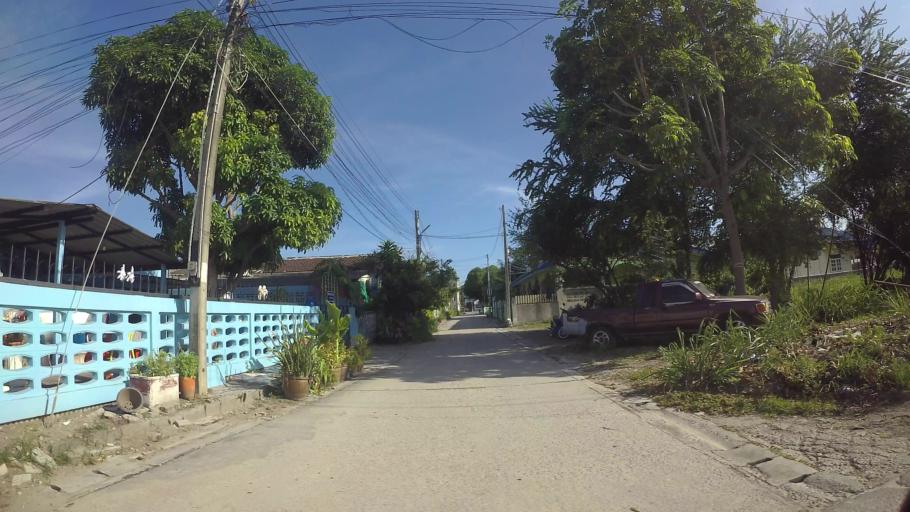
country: TH
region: Rayong
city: Rayong
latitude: 12.6658
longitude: 101.3014
